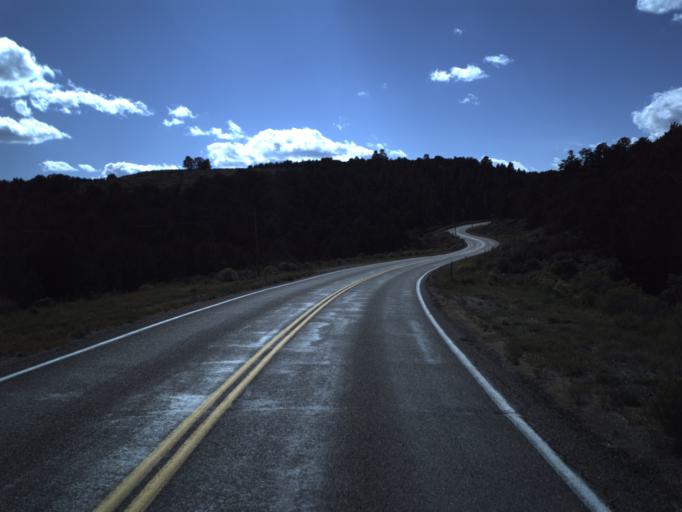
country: US
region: Utah
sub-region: Garfield County
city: Panguitch
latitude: 37.7706
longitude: -112.4479
